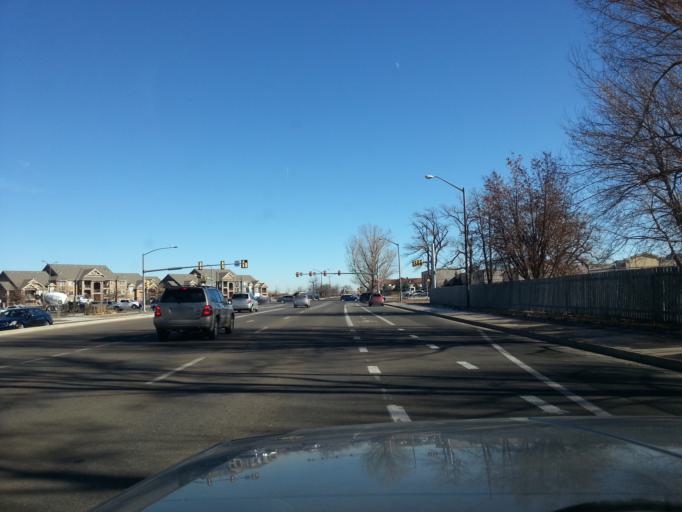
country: US
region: Colorado
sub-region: Larimer County
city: Fort Collins
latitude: 40.5526
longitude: -105.0404
